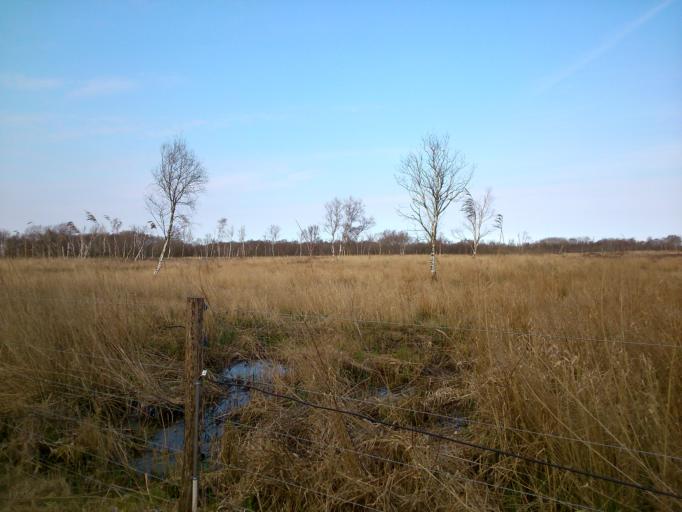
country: DK
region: South Denmark
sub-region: Tonder Kommune
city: Tonder
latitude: 55.0315
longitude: 8.8346
